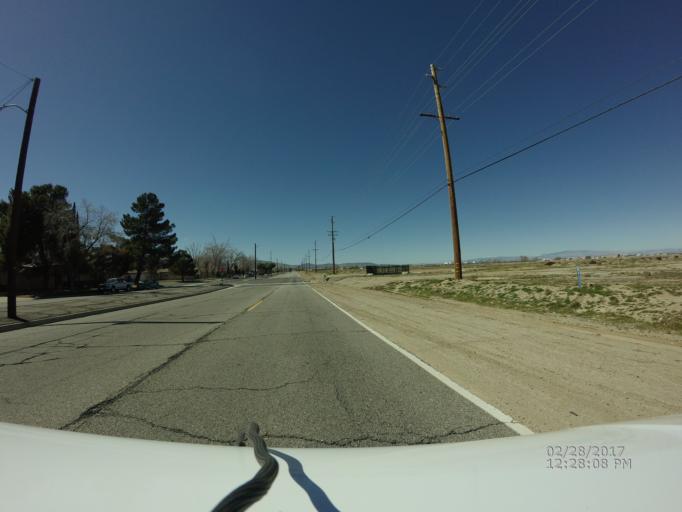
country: US
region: California
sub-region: Los Angeles County
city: Palmdale
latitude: 34.5875
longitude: -118.0668
